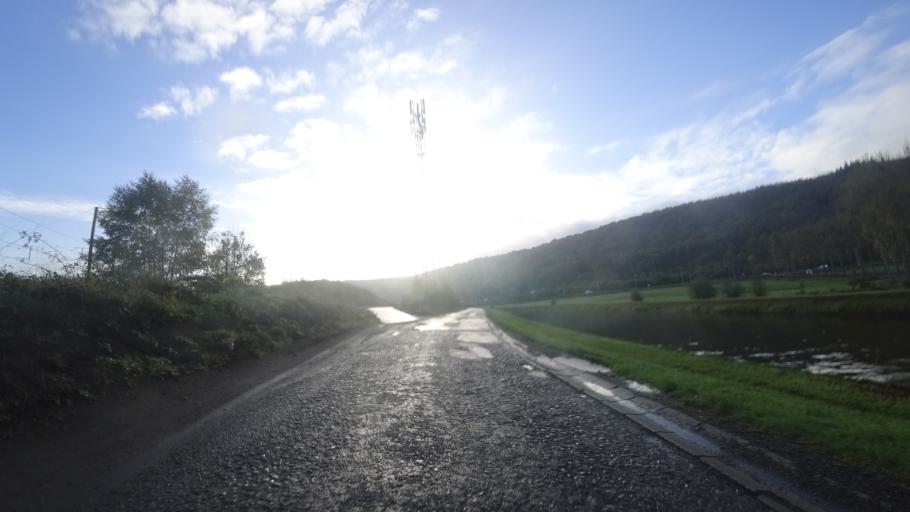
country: BE
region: Wallonia
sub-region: Province de Namur
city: Namur
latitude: 50.4522
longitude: 4.8197
